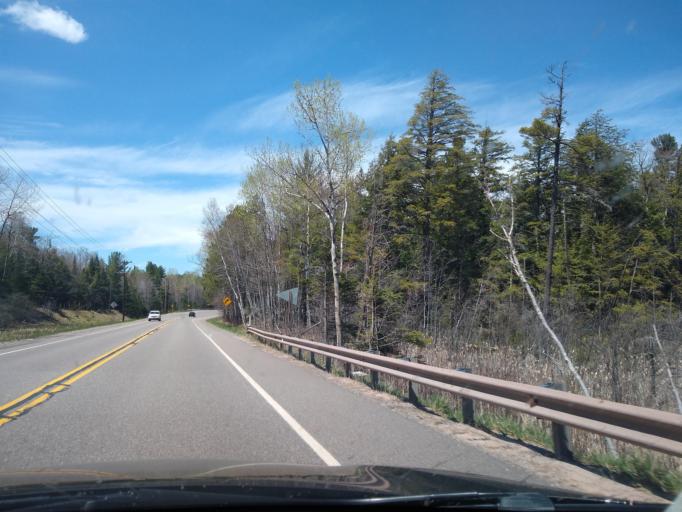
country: US
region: Michigan
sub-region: Marquette County
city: Trowbridge Park
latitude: 46.6060
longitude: -87.4650
